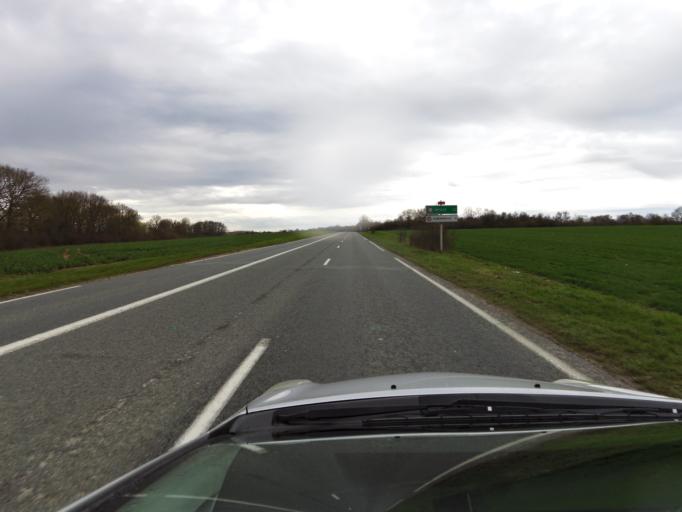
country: FR
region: Picardie
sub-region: Departement de l'Oise
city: Chamant
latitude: 49.1906
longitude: 2.6398
